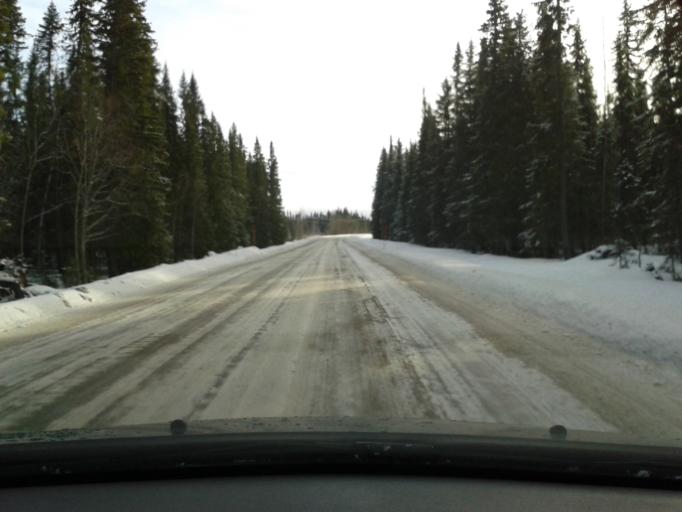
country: SE
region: Vaesterbotten
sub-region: Vilhelmina Kommun
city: Sjoberg
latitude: 64.7372
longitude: 16.2115
